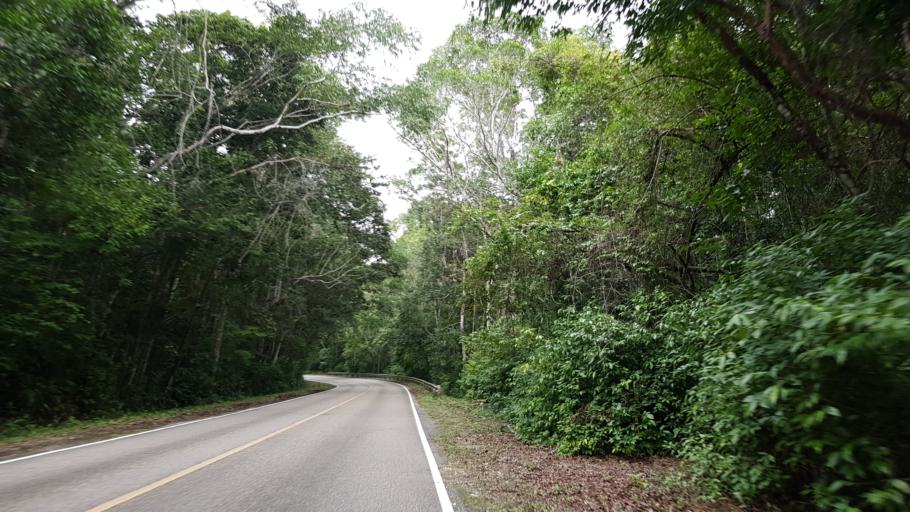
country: GT
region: Peten
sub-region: Municipio de San Jose
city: San Jose
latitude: 17.2136
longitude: -89.6129
